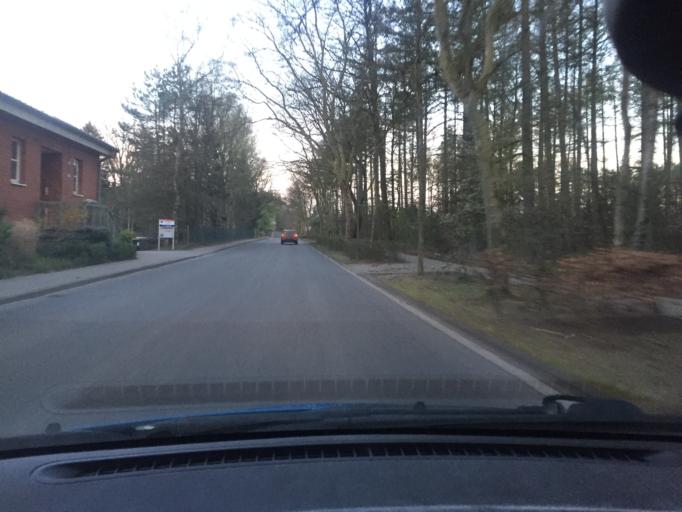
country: DE
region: Lower Saxony
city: Buchholz in der Nordheide
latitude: 53.3148
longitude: 9.8637
